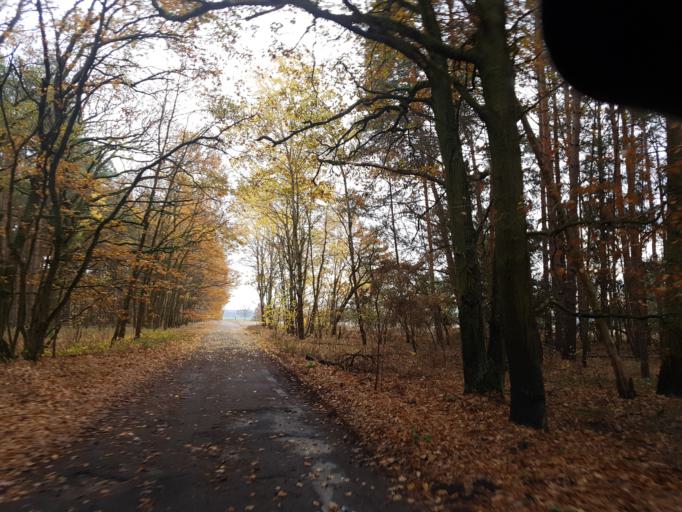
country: DE
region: Brandenburg
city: Treuenbrietzen
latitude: 52.1041
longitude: 12.9190
